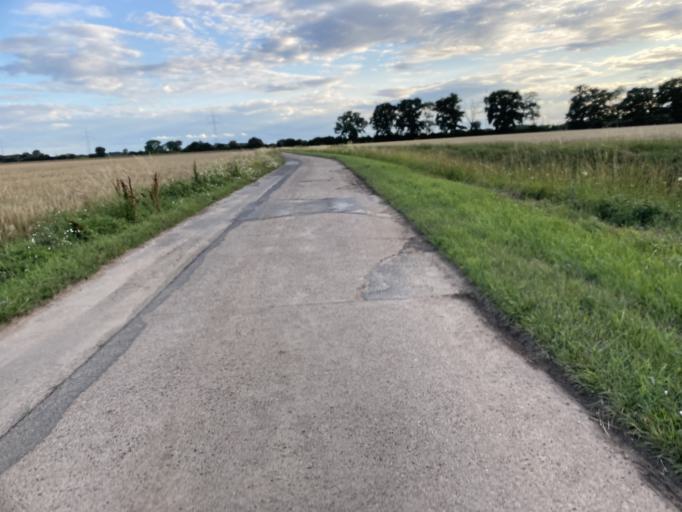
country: DE
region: Lower Saxony
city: Verden
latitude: 52.9135
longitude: 9.1948
